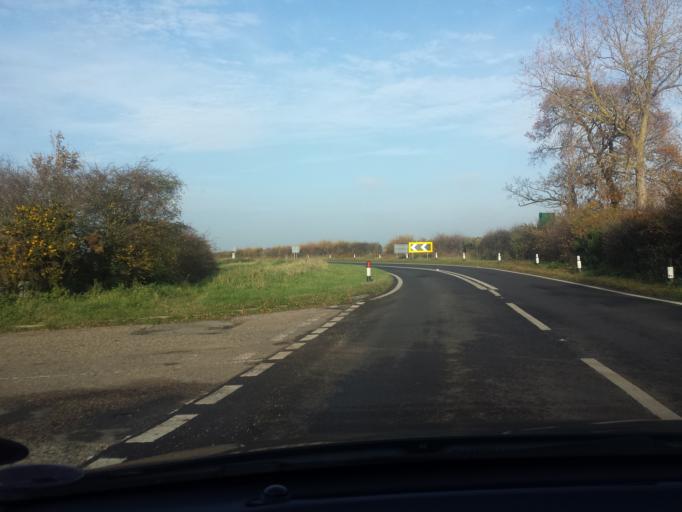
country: GB
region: England
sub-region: Essex
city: Saint Osyth
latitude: 51.8150
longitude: 1.0748
